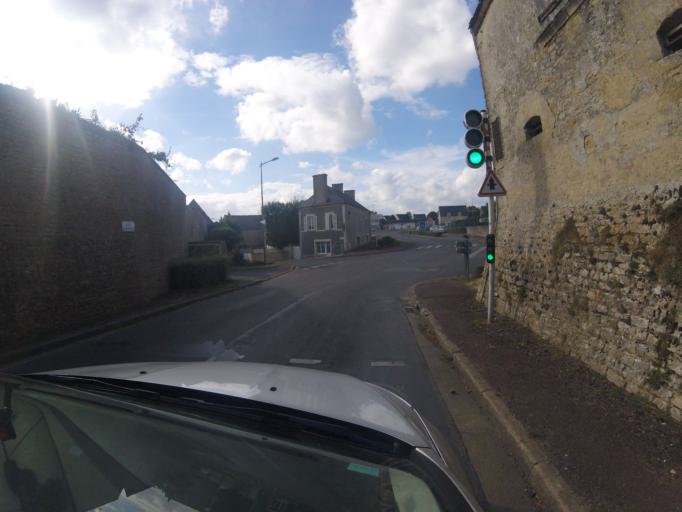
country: FR
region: Lower Normandy
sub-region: Departement du Calvados
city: Saint-Vigor-le-Grand
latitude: 49.3357
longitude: -0.6964
